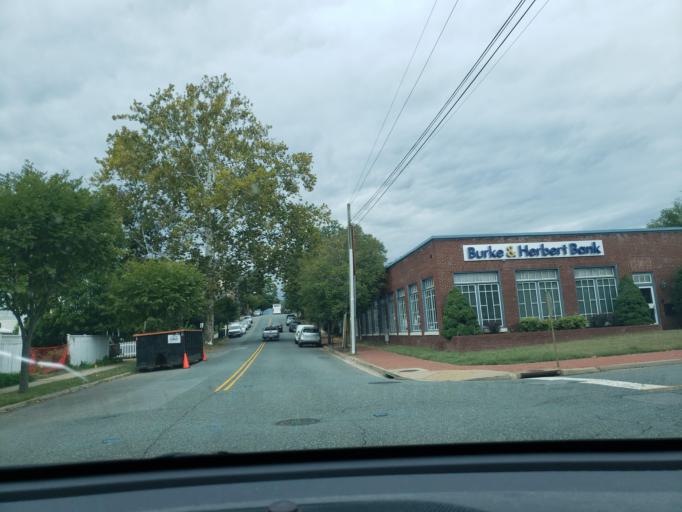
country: US
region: Virginia
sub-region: City of Fredericksburg
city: Fredericksburg
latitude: 38.2985
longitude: -77.4602
